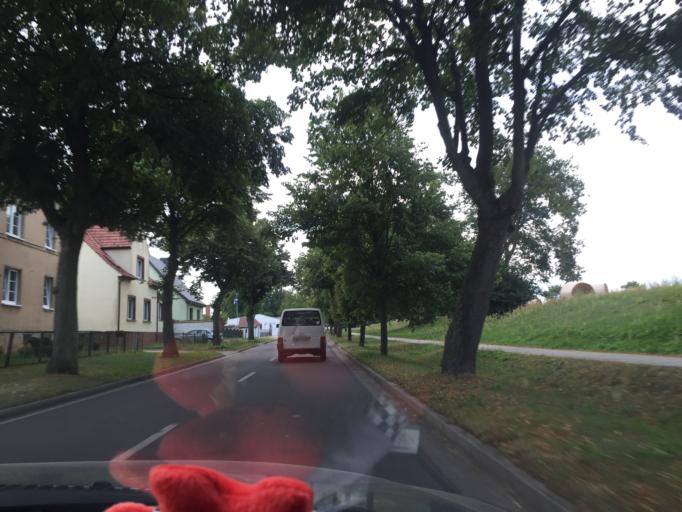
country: DE
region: Brandenburg
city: Zehdenick
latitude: 53.0074
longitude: 13.2952
